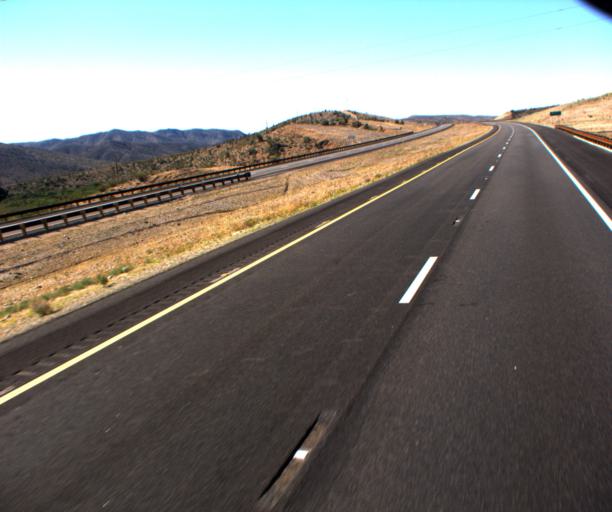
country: US
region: Arizona
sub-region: Mohave County
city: Kingman
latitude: 35.0090
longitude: -113.6646
